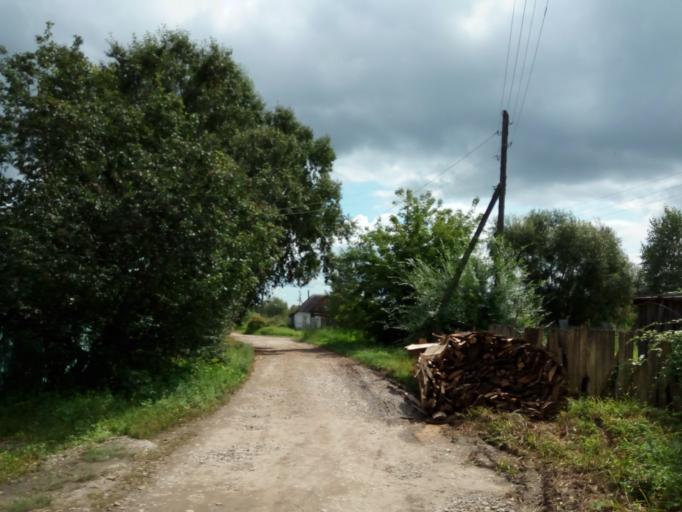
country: RU
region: Primorskiy
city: Dal'nerechensk
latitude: 45.9389
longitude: 133.8142
